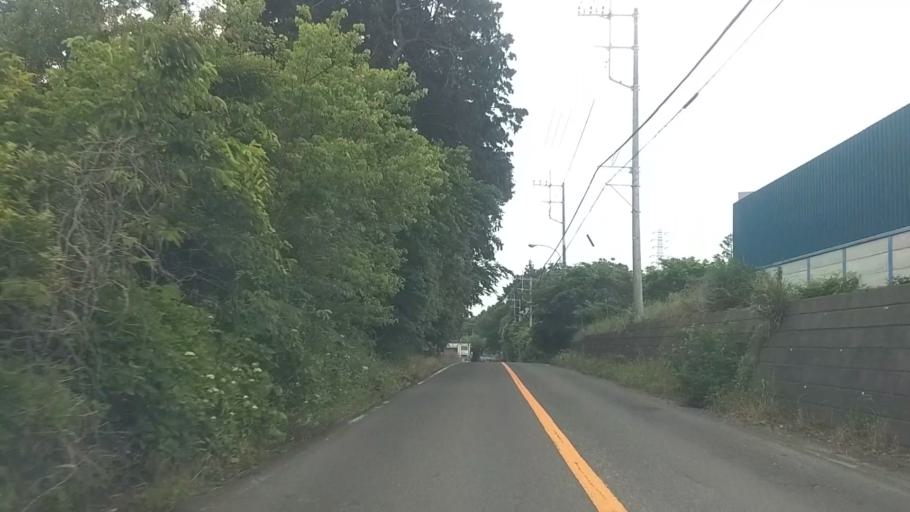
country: JP
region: Kanagawa
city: Fujisawa
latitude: 35.3565
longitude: 139.4352
